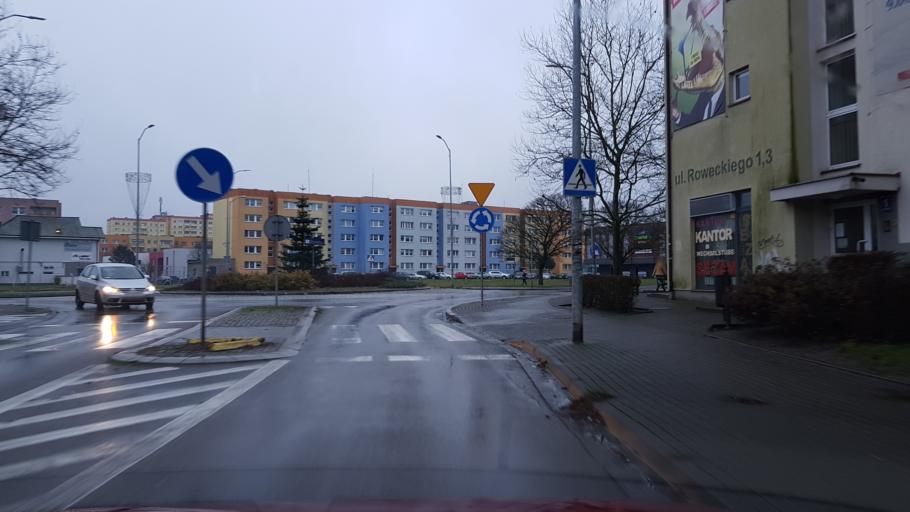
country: PL
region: West Pomeranian Voivodeship
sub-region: Powiat policki
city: Police
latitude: 53.5409
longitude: 14.5468
